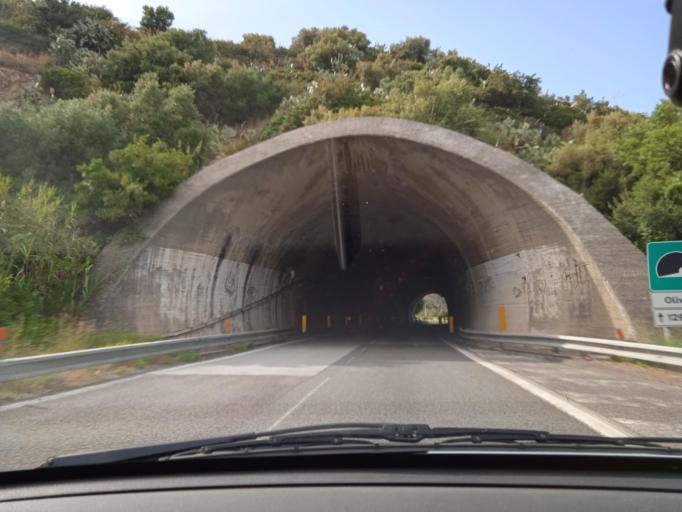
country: IT
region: Sicily
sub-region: Messina
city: Oliveri
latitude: 38.1225
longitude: 15.0551
